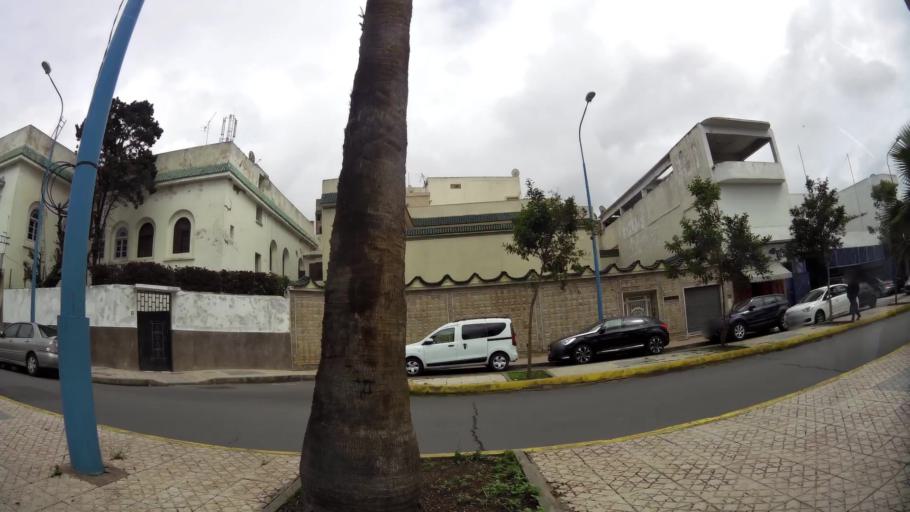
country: MA
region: Grand Casablanca
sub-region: Casablanca
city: Casablanca
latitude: 33.5753
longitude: -7.6098
